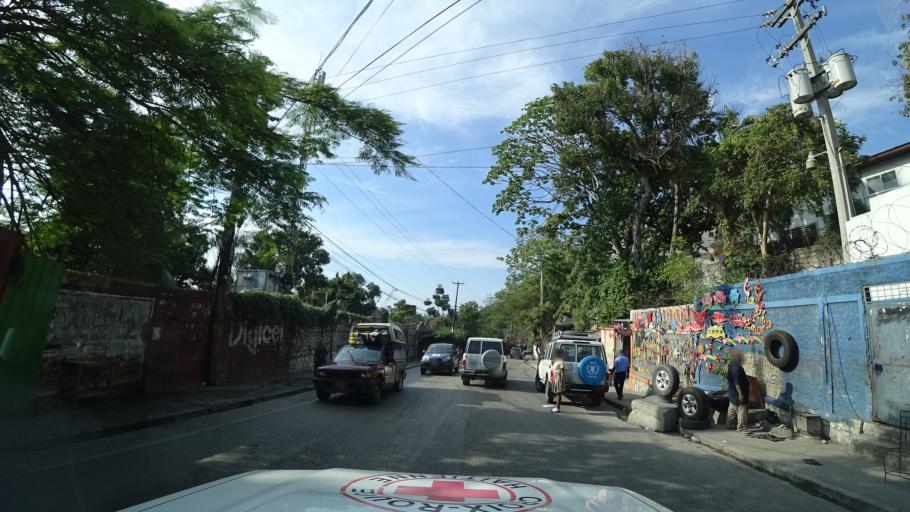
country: HT
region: Ouest
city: Delmas 73
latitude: 18.5307
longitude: -72.3009
